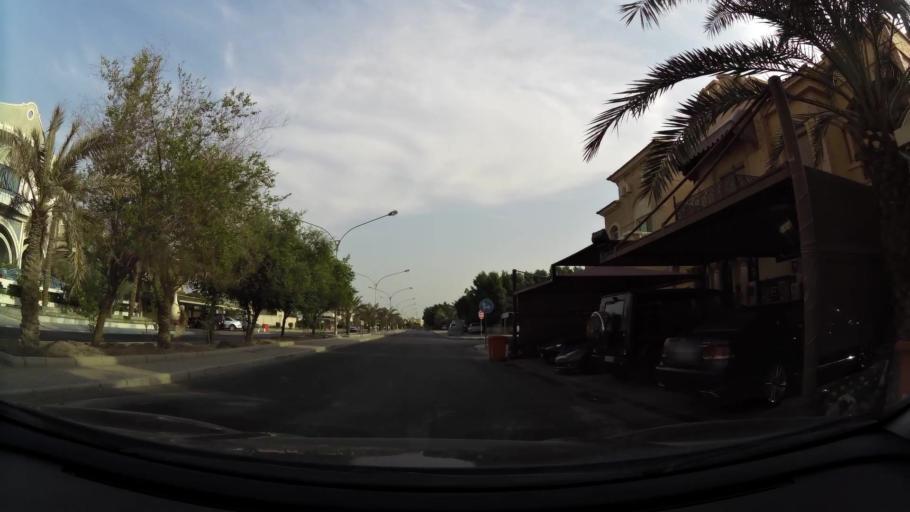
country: KW
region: Muhafazat Hawalli
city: Hawalli
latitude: 29.3140
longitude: 48.0111
